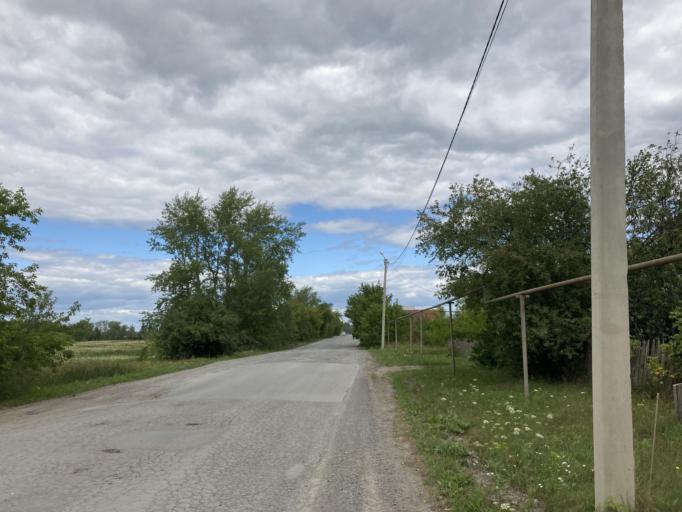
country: RU
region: Sverdlovsk
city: Bogdanovich
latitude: 56.7887
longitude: 62.0667
